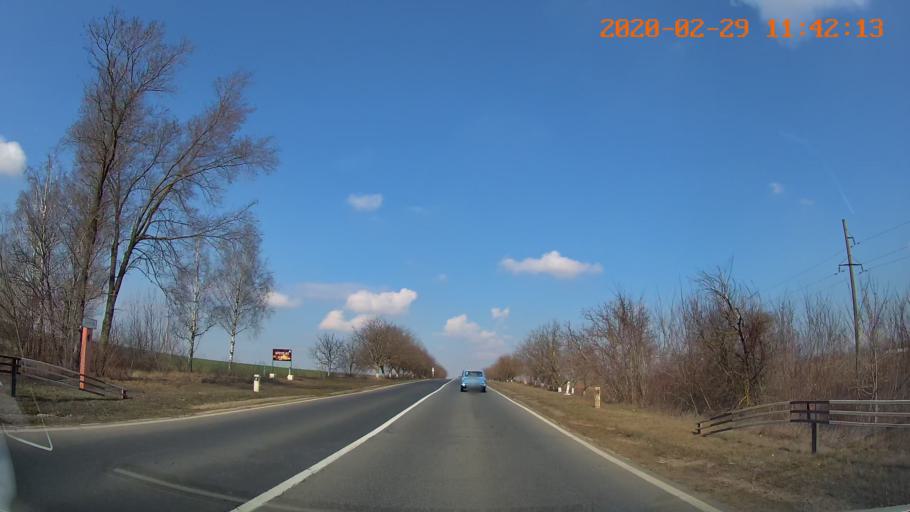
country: MD
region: Rezina
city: Saharna
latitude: 47.6811
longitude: 29.0137
